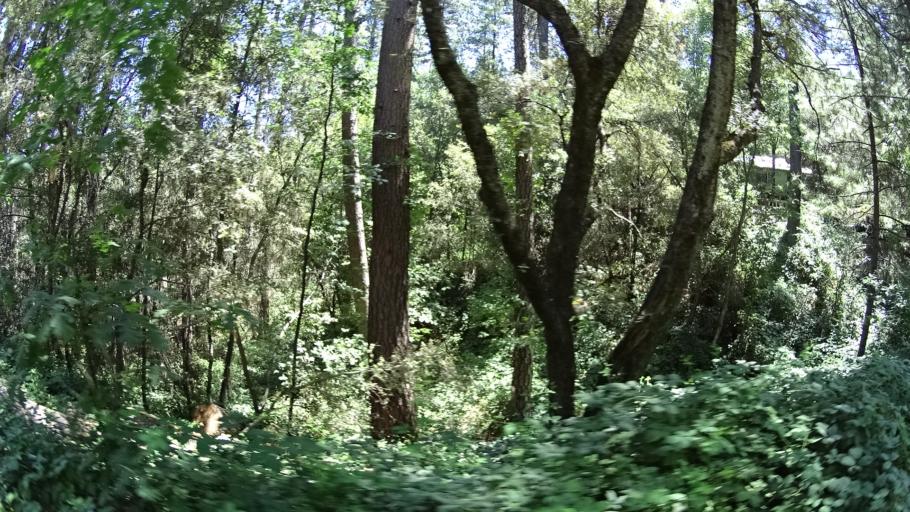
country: US
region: California
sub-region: Calaveras County
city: Forest Meadows
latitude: 38.1554
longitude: -120.4013
